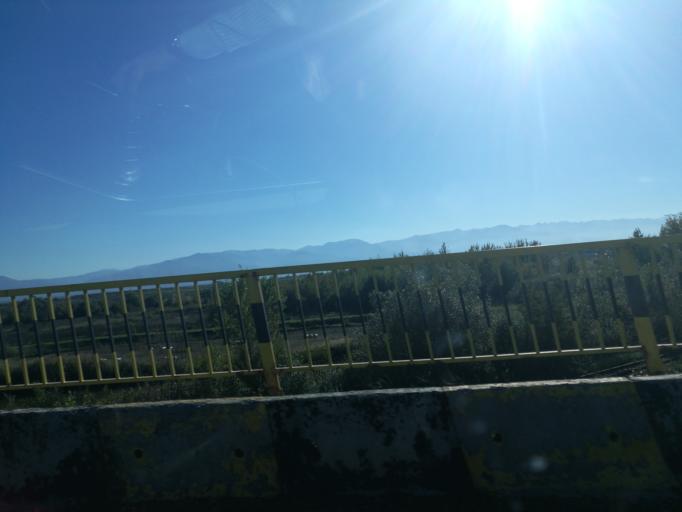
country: RO
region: Brasov
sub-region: Comuna Mandra
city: Mandra
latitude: 45.8316
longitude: 25.0164
